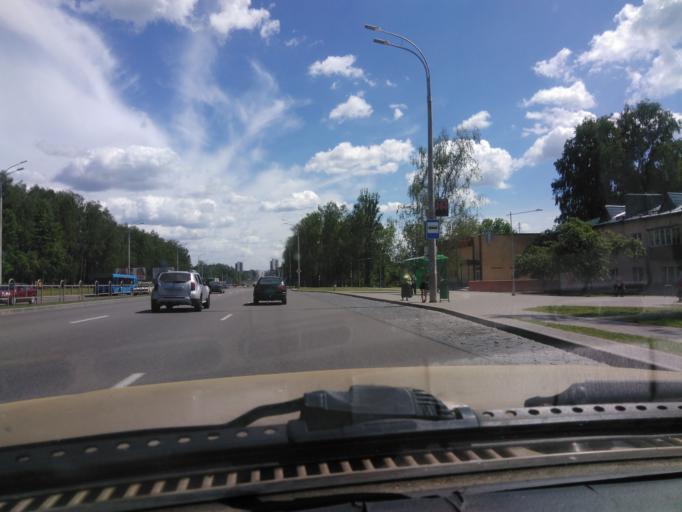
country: BY
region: Mogilev
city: Buynichy
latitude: 53.9301
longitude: 30.2640
